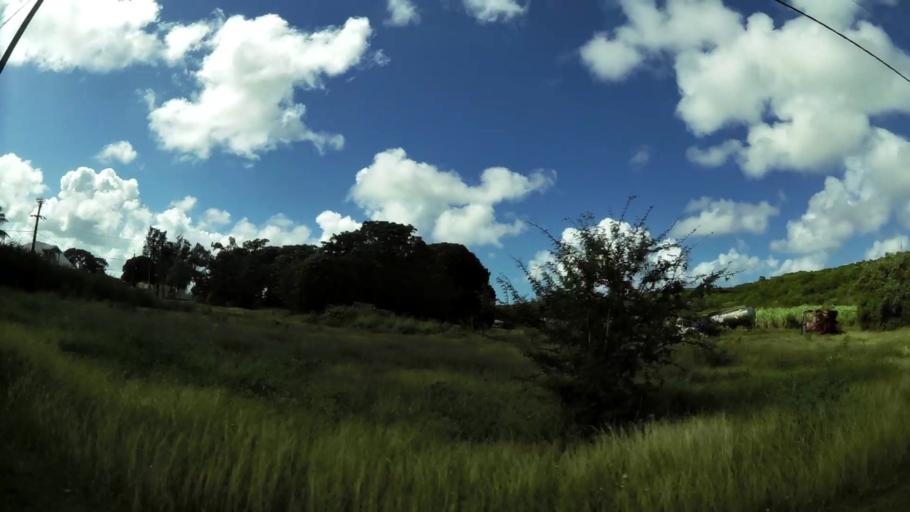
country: GP
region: Guadeloupe
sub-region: Guadeloupe
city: Anse-Bertrand
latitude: 16.4315
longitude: -61.4771
